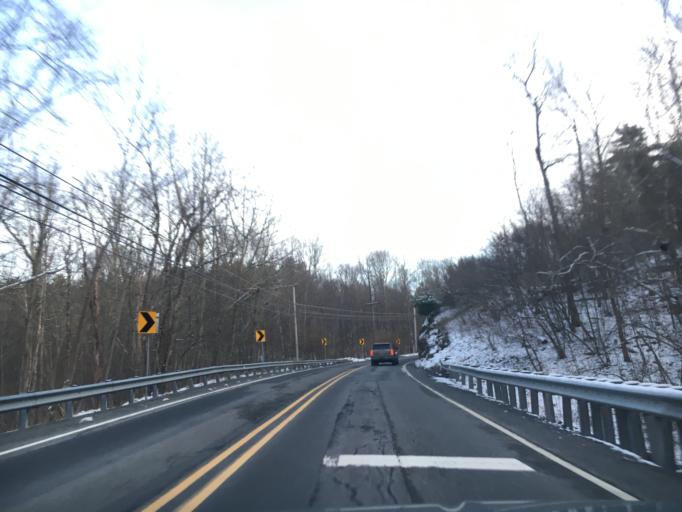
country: US
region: Pennsylvania
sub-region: Pike County
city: Saw Creek
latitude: 41.1027
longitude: -75.0976
